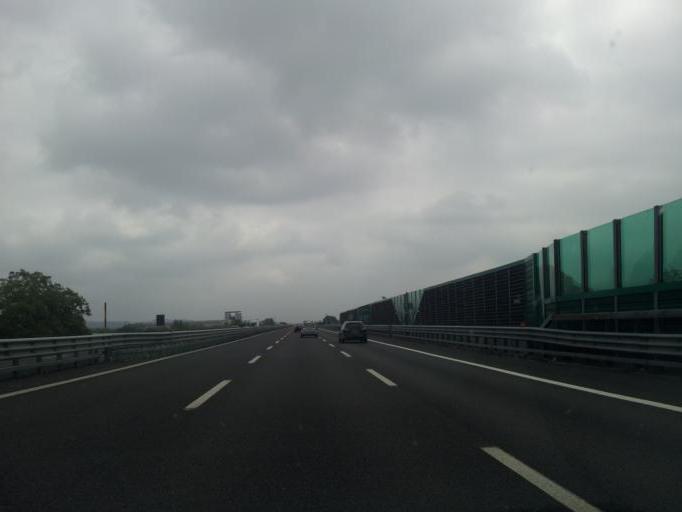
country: IT
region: Veneto
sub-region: Provincia di Verona
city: Monticelli-Fontana
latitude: 45.4218
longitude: 11.1378
